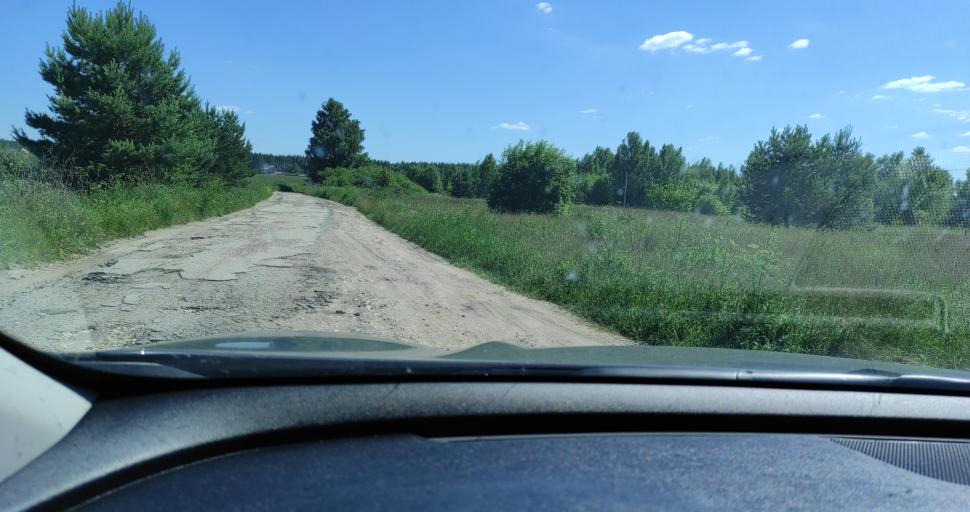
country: RU
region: Rjazan
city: Murmino
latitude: 54.5670
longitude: 40.0954
